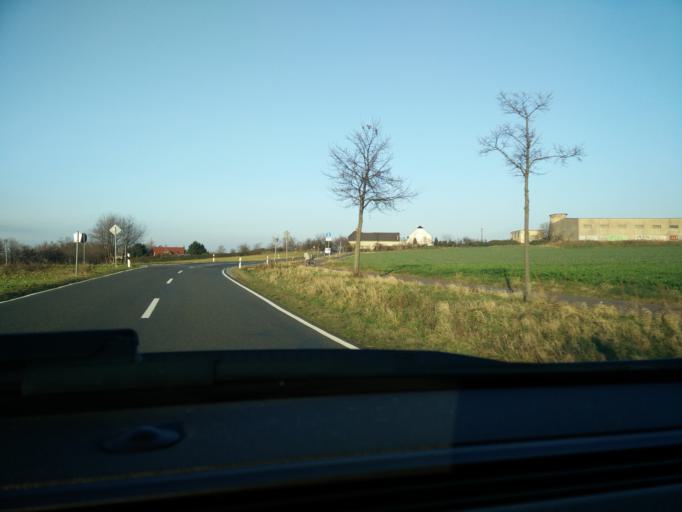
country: DE
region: Saxony
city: Grossbardau
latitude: 51.1964
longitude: 12.6989
